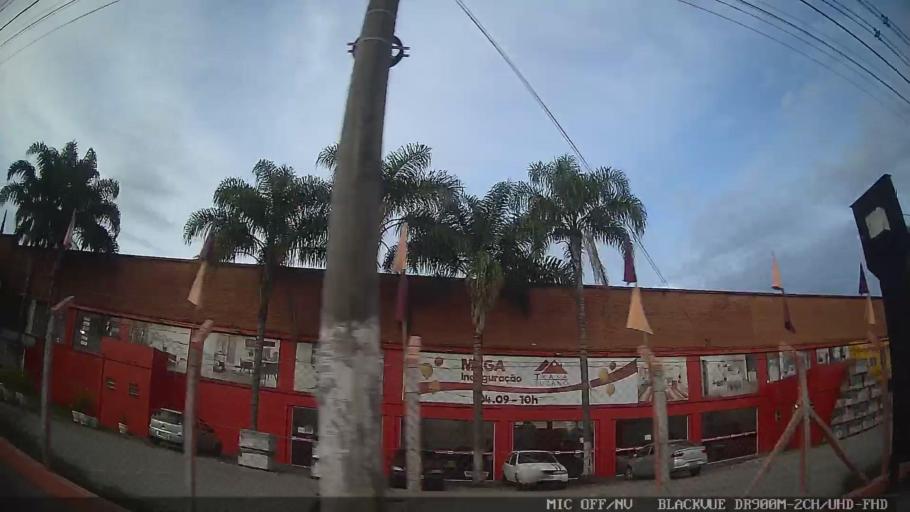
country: BR
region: Sao Paulo
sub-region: Suzano
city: Suzano
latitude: -23.5375
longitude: -46.2999
